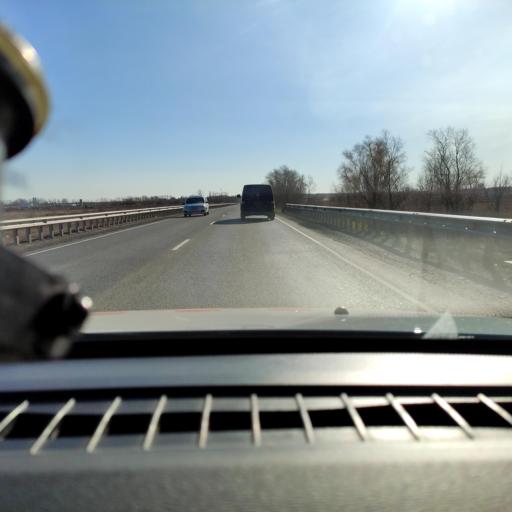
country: RU
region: Samara
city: Samara
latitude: 53.0967
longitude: 50.1452
